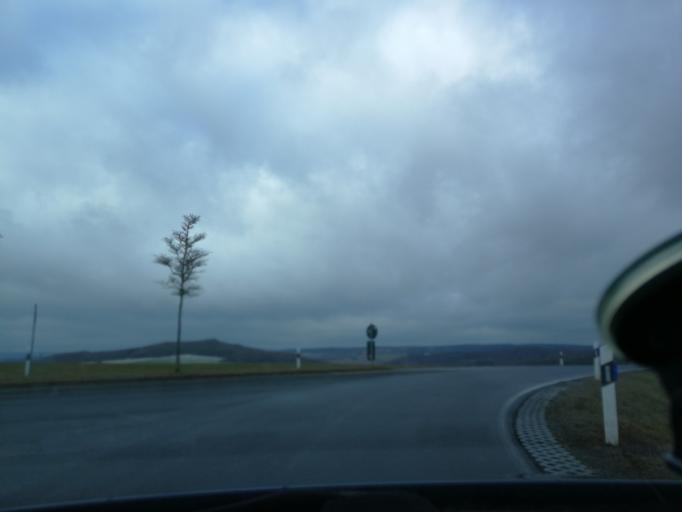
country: DE
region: Rheinland-Pfalz
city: Oberehe-Stroheich
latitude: 50.2799
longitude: 6.7537
